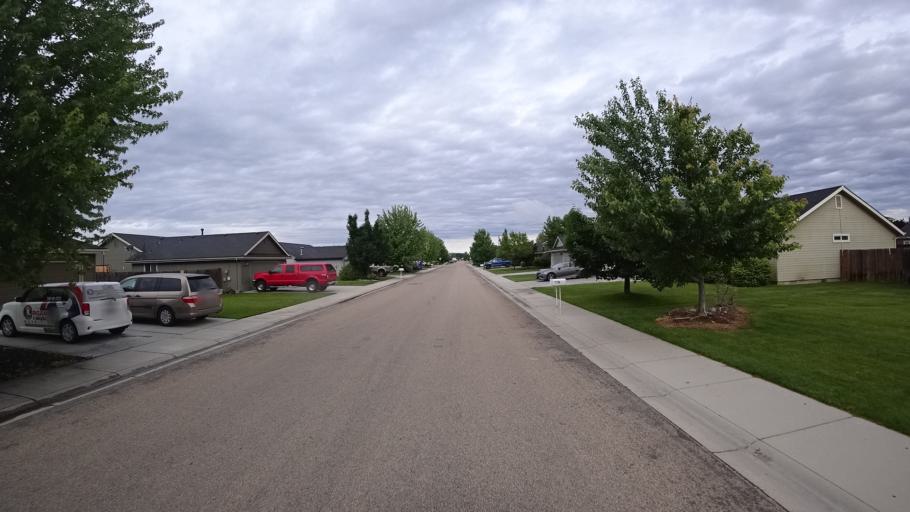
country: US
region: Idaho
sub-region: Ada County
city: Star
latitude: 43.6961
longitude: -116.5009
